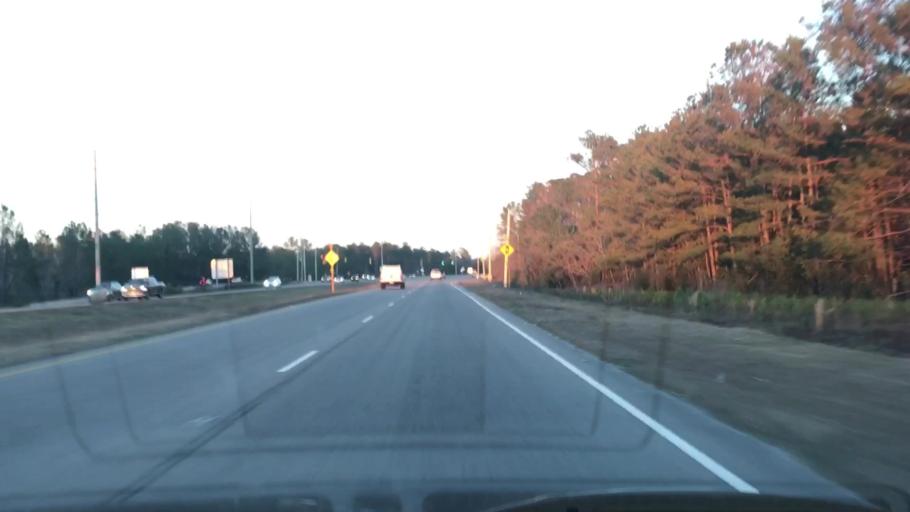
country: US
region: North Carolina
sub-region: Brunswick County
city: Shallotte
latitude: 33.9861
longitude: -78.3921
